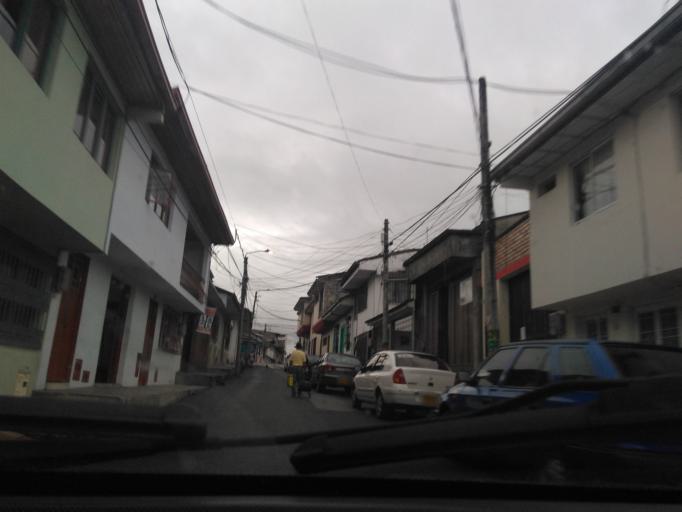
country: CO
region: Cauca
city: Popayan
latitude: 2.4448
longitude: -76.6114
